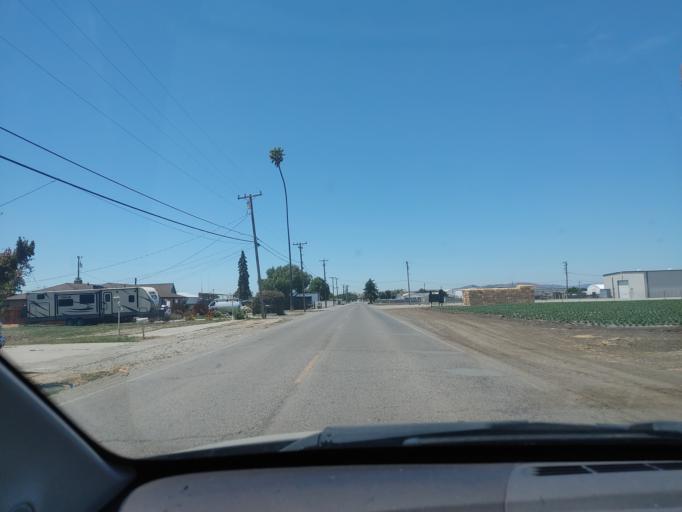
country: US
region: California
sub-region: San Benito County
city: Hollister
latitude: 36.8692
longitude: -121.3961
